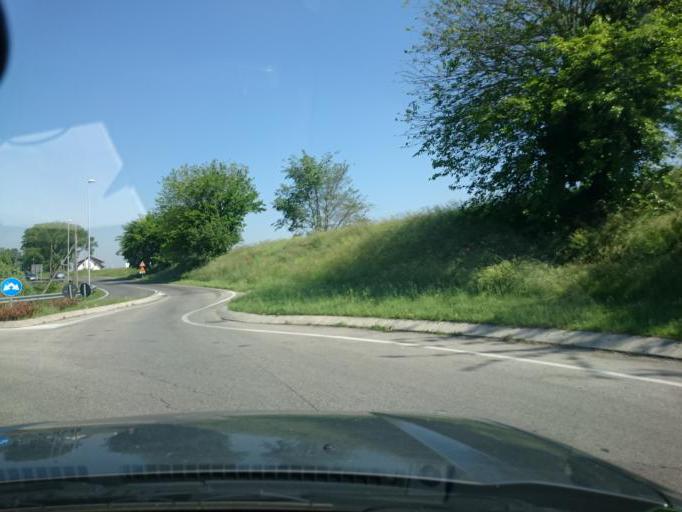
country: IT
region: Veneto
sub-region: Provincia di Padova
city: Oltre Brenta
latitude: 45.4069
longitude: 11.9976
